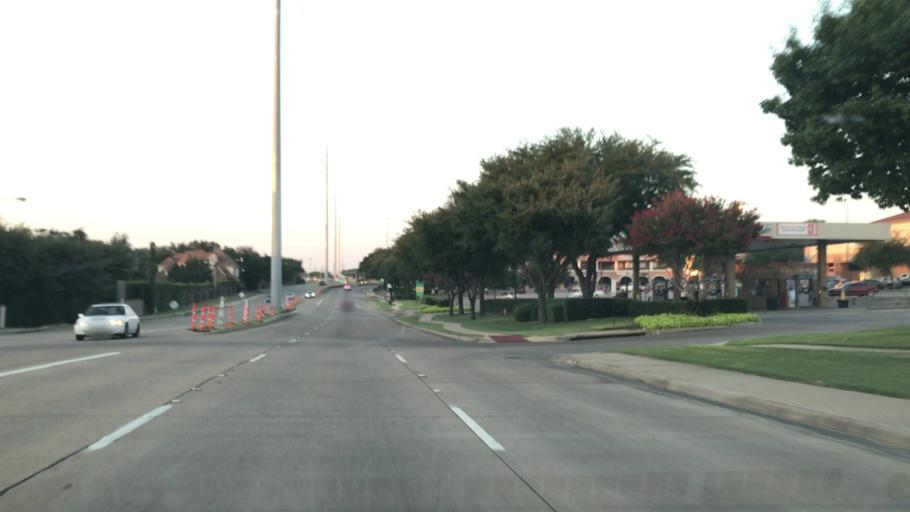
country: US
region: Texas
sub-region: Dallas County
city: Richardson
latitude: 32.8961
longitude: -96.7225
